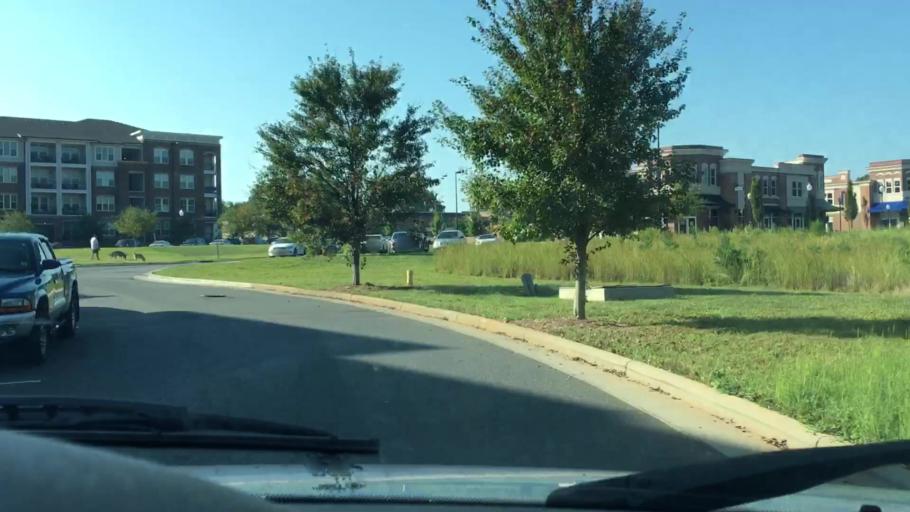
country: US
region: North Carolina
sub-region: Mecklenburg County
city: Cornelius
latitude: 35.4822
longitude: -80.8553
